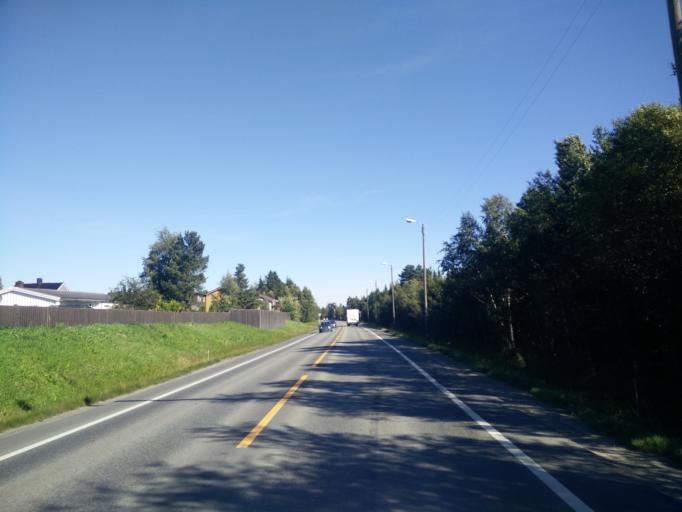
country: NO
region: Sor-Trondelag
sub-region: Trondheim
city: Trondheim
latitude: 63.3447
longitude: 10.3680
